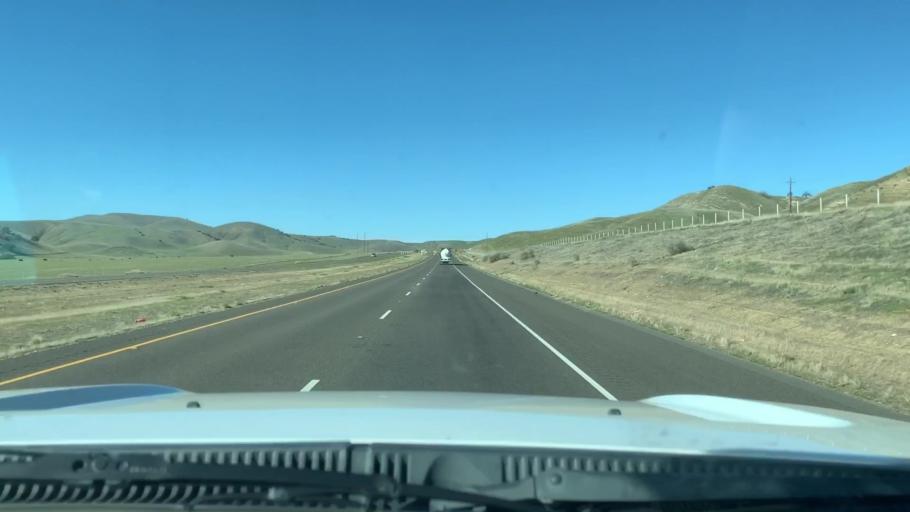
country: US
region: California
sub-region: San Luis Obispo County
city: Shandon
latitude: 35.7201
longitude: -120.1809
